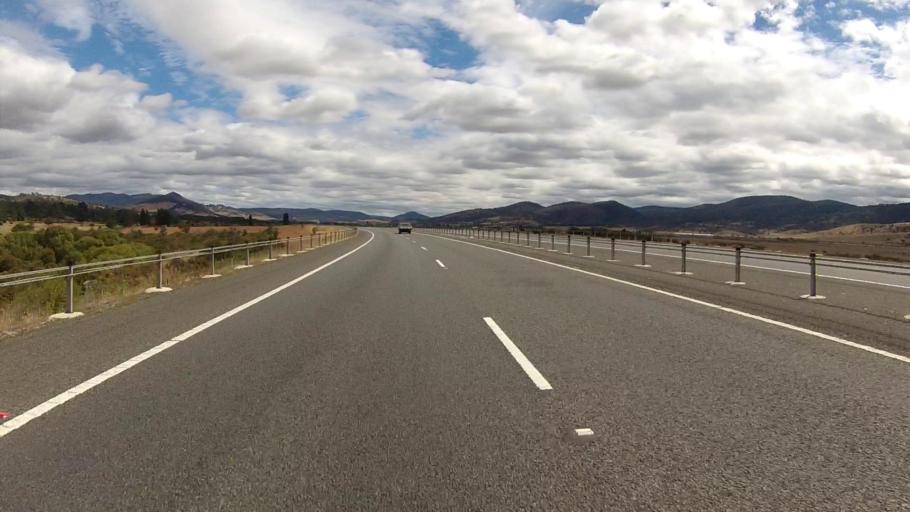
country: AU
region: Tasmania
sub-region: Brighton
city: Bridgewater
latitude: -42.6837
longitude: 147.2772
